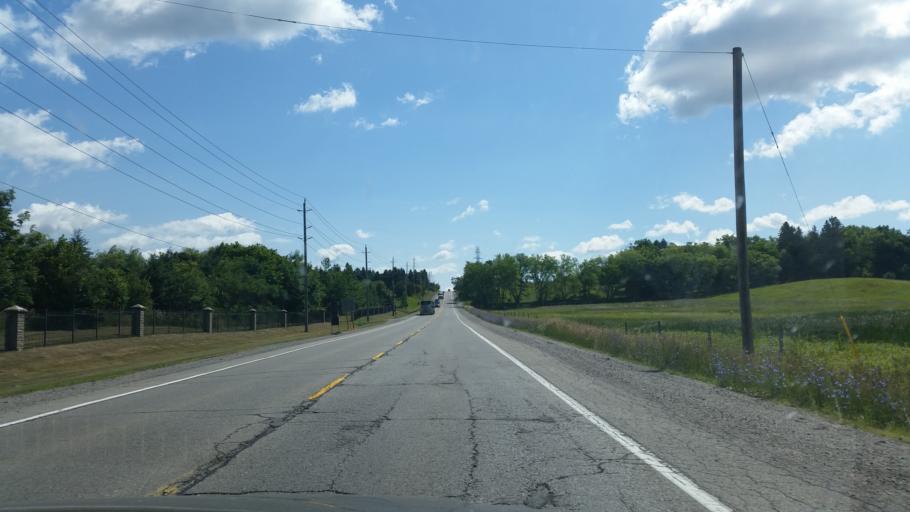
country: CA
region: Ontario
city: Vaughan
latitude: 43.9082
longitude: -79.6237
